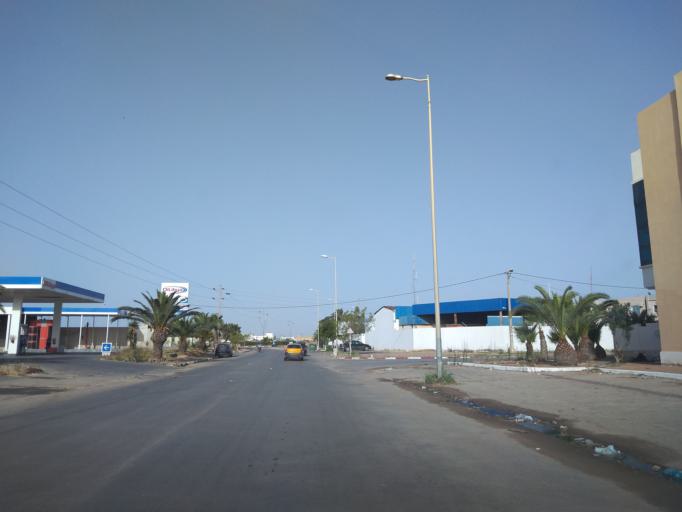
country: TN
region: Safaqis
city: Sfax
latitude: 34.7283
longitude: 10.7520
